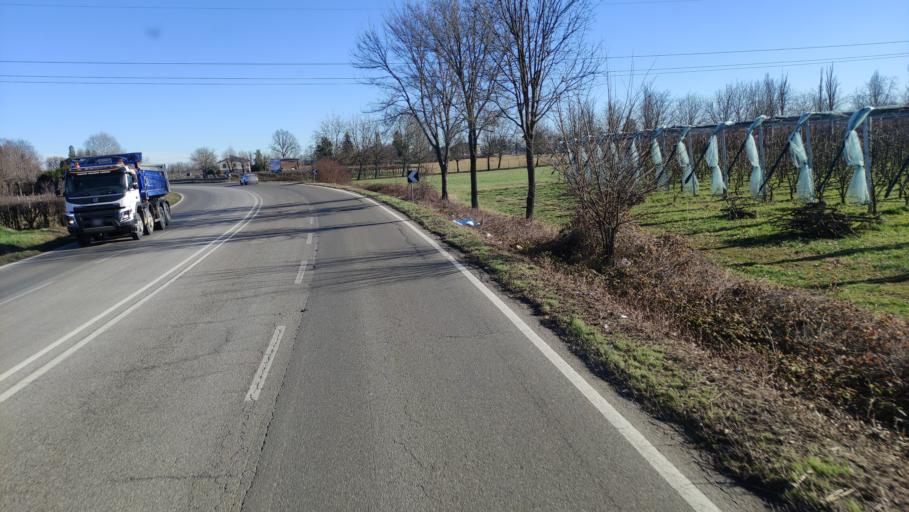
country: IT
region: Emilia-Romagna
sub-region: Provincia di Reggio Emilia
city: Correggio
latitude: 44.7601
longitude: 10.8048
